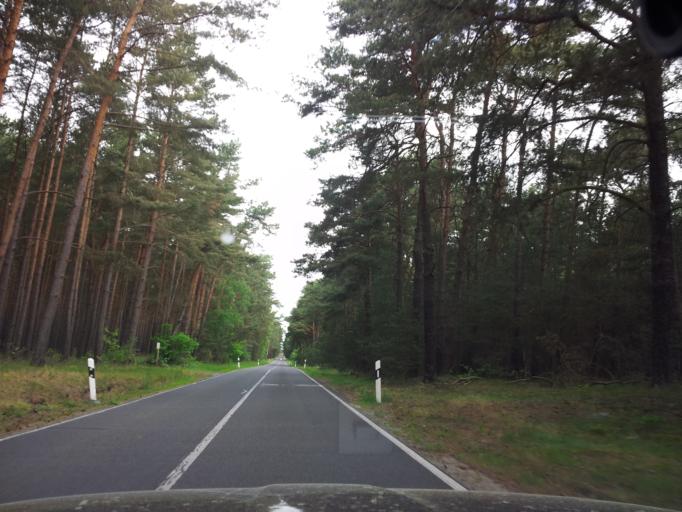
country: DE
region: Brandenburg
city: Treuenbrietzen
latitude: 52.0814
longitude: 12.8032
